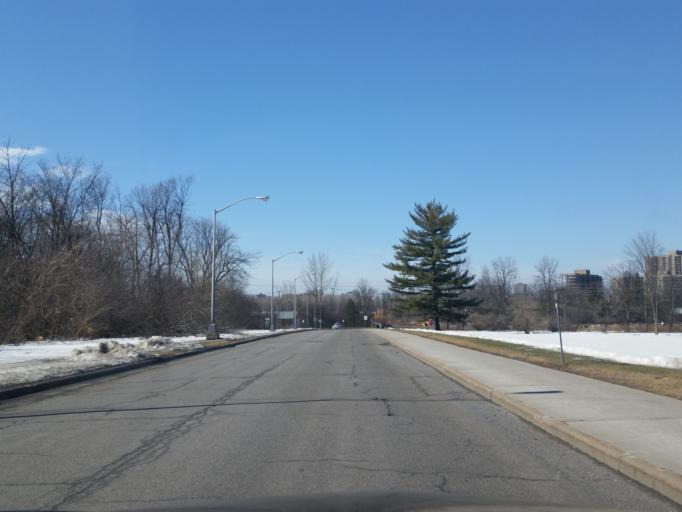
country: CA
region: Ontario
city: Ottawa
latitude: 45.4018
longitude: -75.6595
